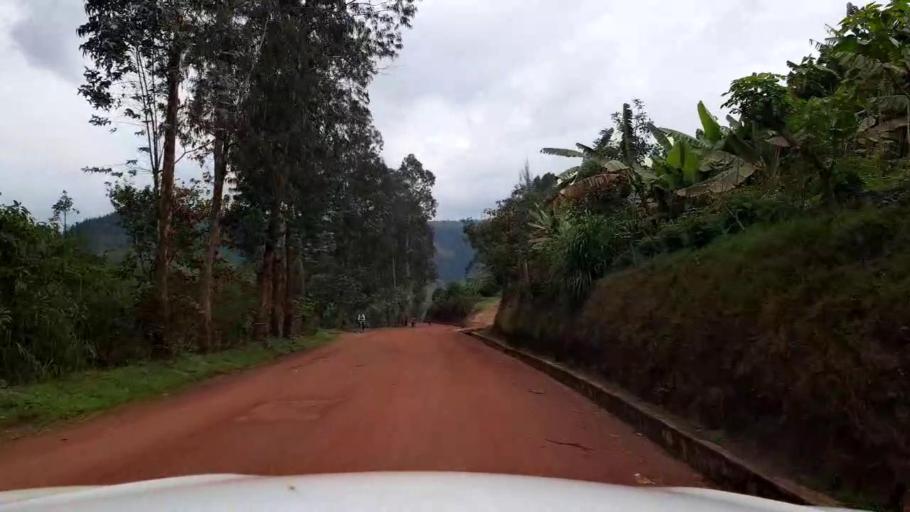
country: RW
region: Northern Province
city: Musanze
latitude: -1.6621
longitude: 29.8014
